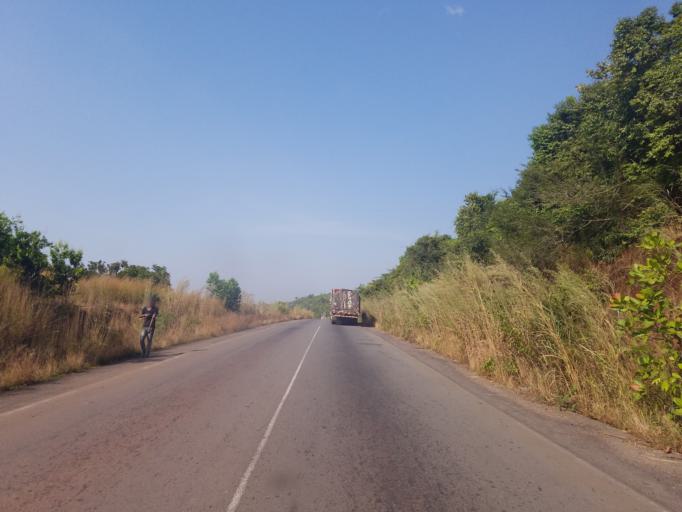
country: GN
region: Boke
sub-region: Boffa
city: Boffa
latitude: 10.1396
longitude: -13.9848
